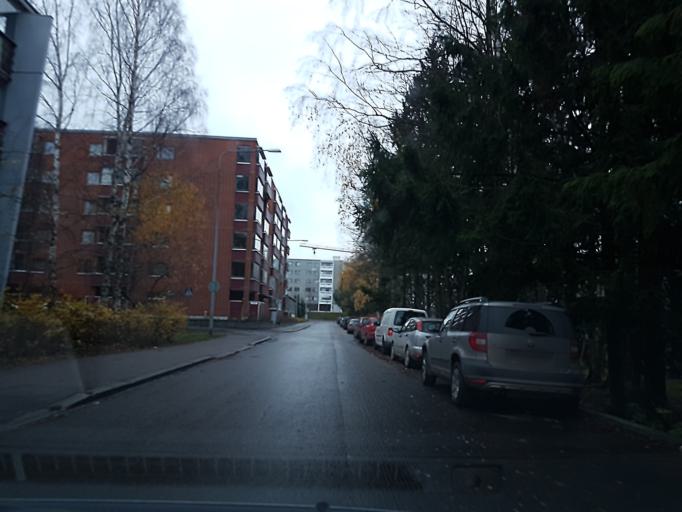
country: FI
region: Uusimaa
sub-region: Helsinki
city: Vantaa
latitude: 60.2388
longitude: 25.1125
